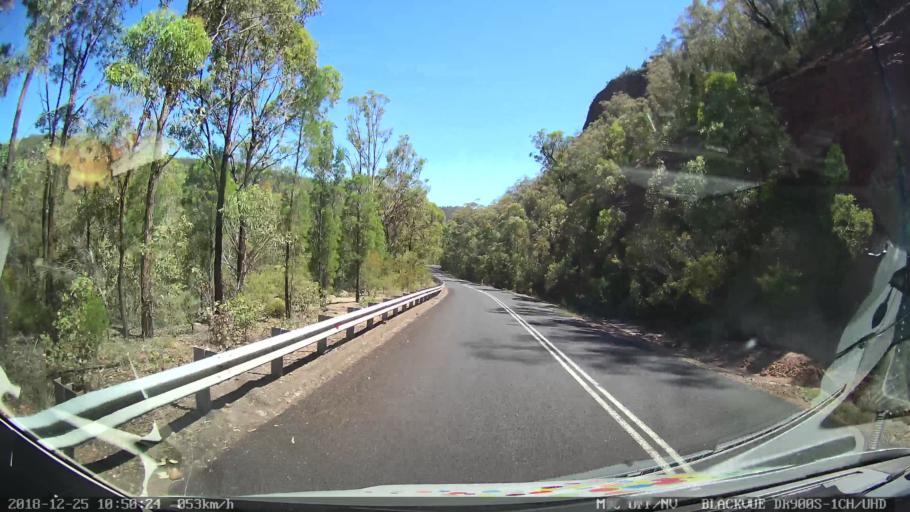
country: AU
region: New South Wales
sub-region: Upper Hunter Shire
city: Merriwa
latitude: -32.4463
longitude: 150.2681
